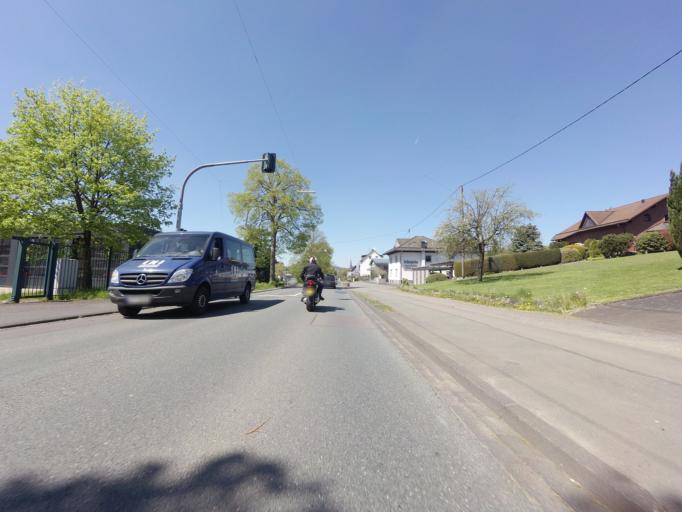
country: DE
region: North Rhine-Westphalia
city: Kreuztal
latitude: 50.9592
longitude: 8.0171
